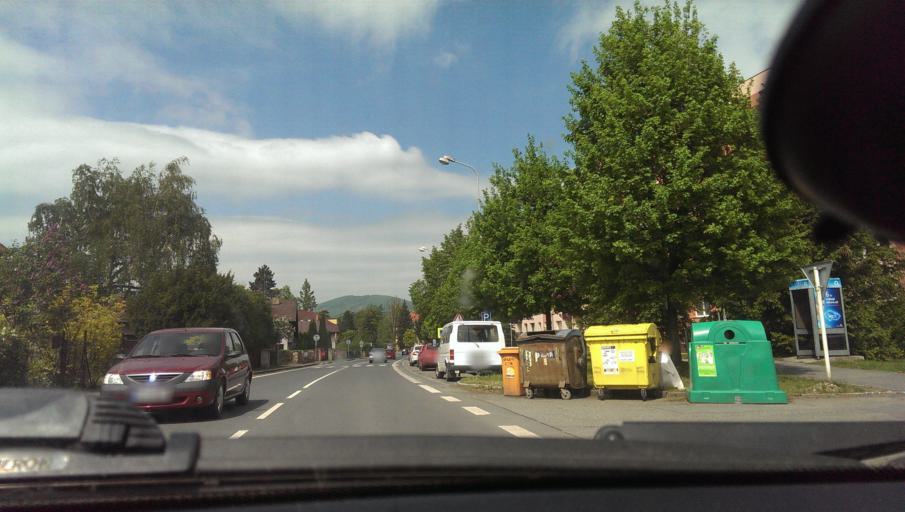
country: CZ
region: Moravskoslezsky
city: Frenstat pod Radhostem
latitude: 49.5491
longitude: 18.2055
